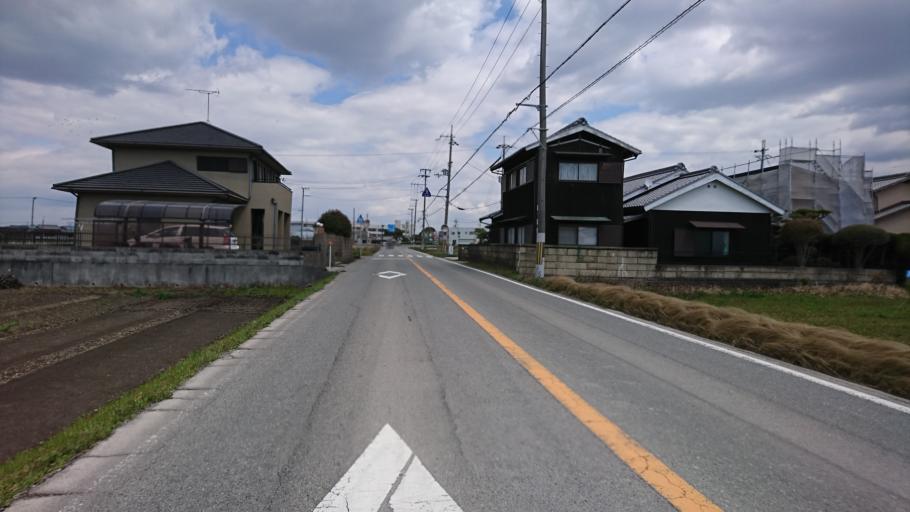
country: JP
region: Hyogo
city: Miki
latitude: 34.7515
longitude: 134.9405
